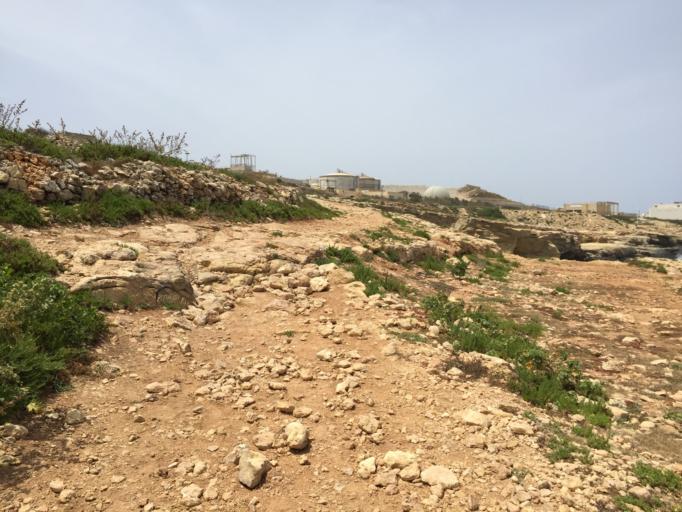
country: MT
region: Ix-Xghajra
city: Xghajra
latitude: 35.8810
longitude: 14.5586
